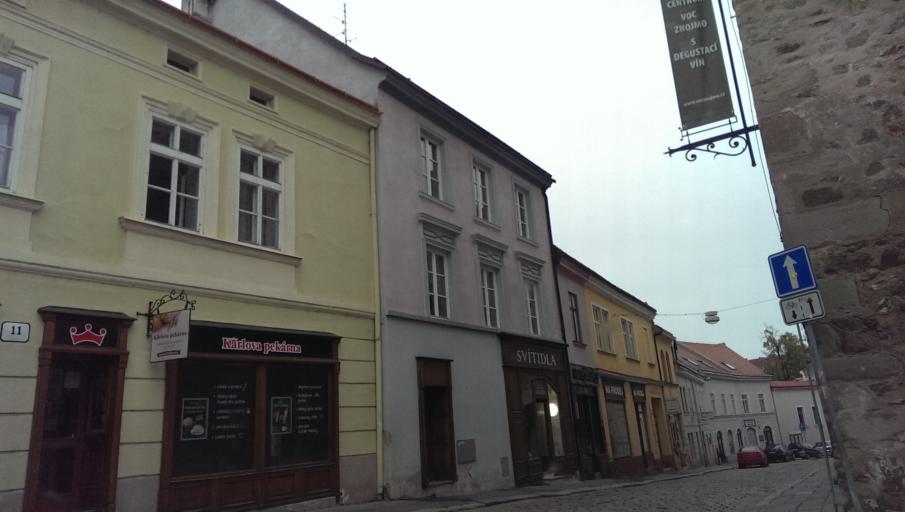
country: CZ
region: South Moravian
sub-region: Okres Znojmo
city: Znojmo
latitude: 48.8537
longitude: 16.0511
